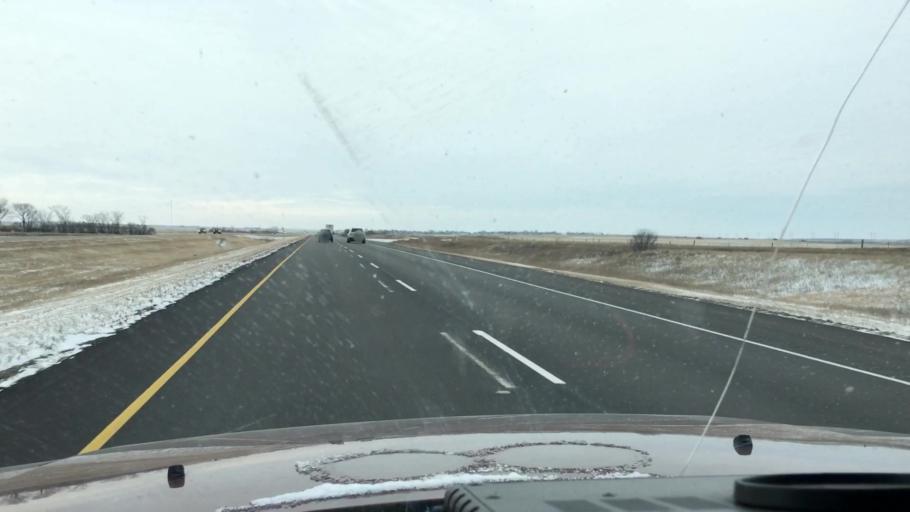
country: CA
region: Saskatchewan
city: Saskatoon
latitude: 51.8407
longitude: -106.5045
